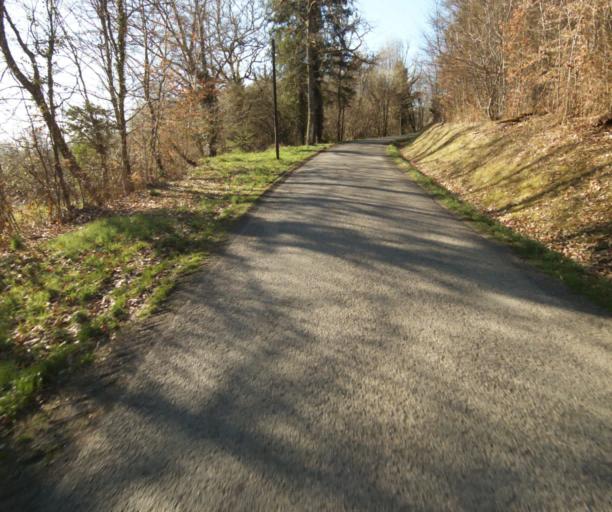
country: FR
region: Limousin
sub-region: Departement de la Correze
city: Seilhac
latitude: 45.3906
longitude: 1.7585
